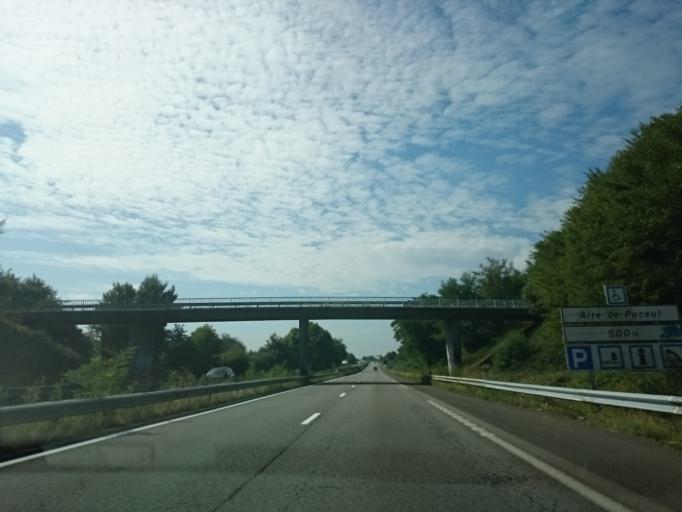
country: FR
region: Pays de la Loire
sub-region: Departement de la Loire-Atlantique
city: Nozay
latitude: 47.5434
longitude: -1.6355
